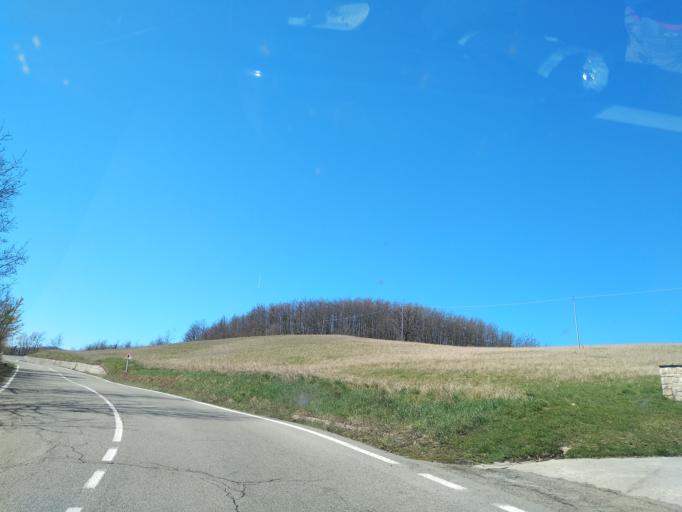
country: IT
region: Emilia-Romagna
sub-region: Provincia di Reggio Emilia
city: Castelnovo ne'Monti
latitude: 44.4217
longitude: 10.3703
